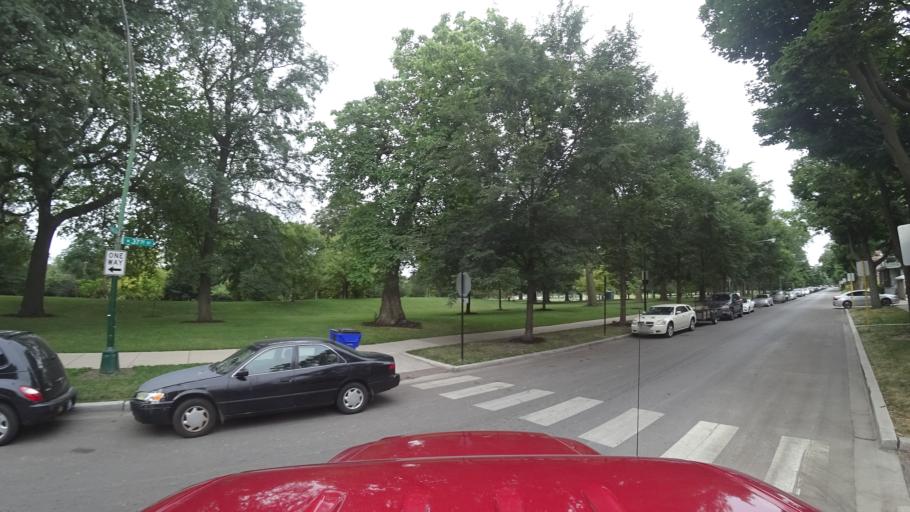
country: US
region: Illinois
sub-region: Cook County
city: Chicago
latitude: 41.8268
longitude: -87.6789
